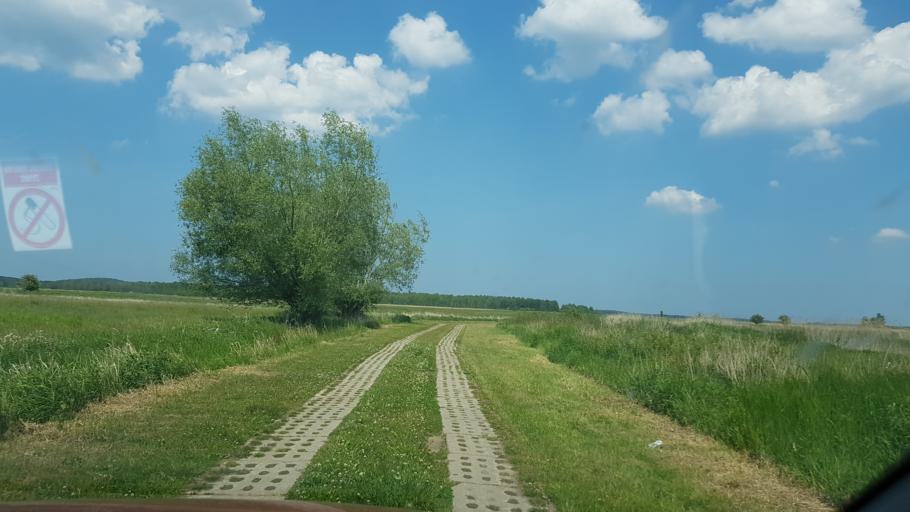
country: PL
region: West Pomeranian Voivodeship
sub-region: Powiat gryficki
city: Trzebiatow
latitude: 54.0944
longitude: 15.2127
